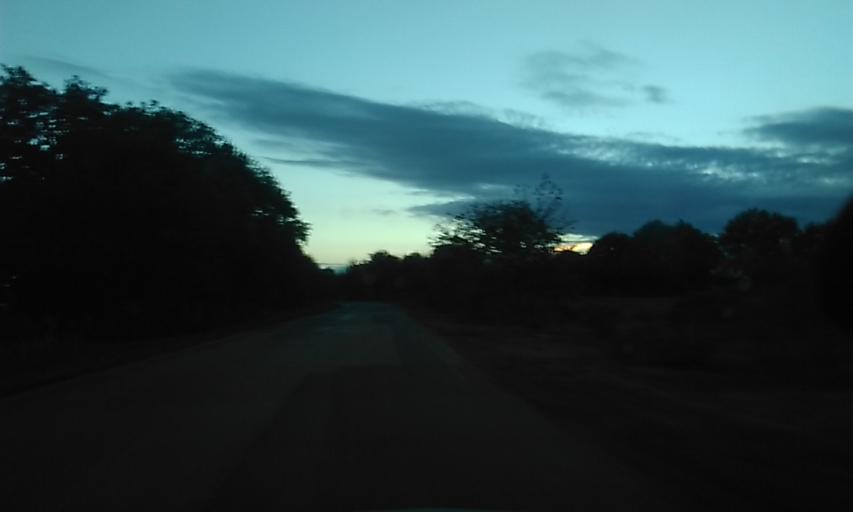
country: FR
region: Brittany
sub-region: Departement d'Ille-et-Vilaine
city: Saint-Thurial
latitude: 48.0526
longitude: -1.9226
